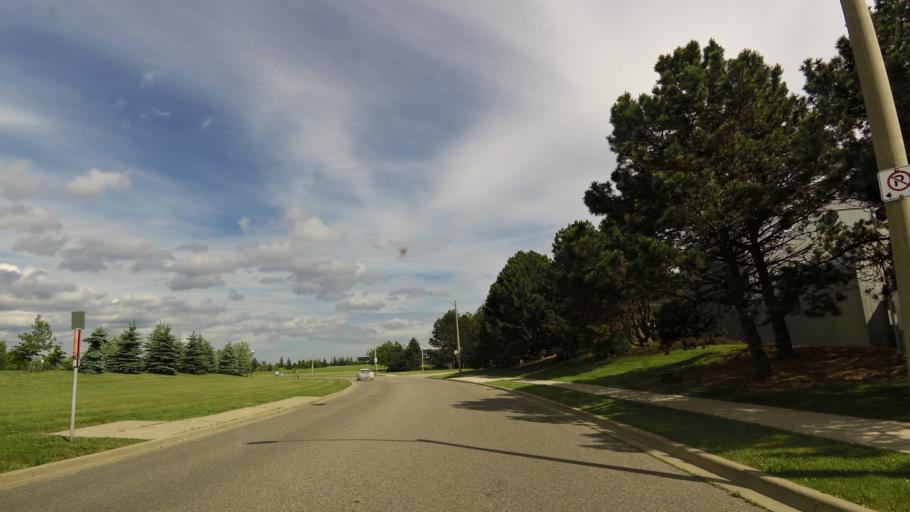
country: CA
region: Ontario
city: Mississauga
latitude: 43.5138
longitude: -79.6668
